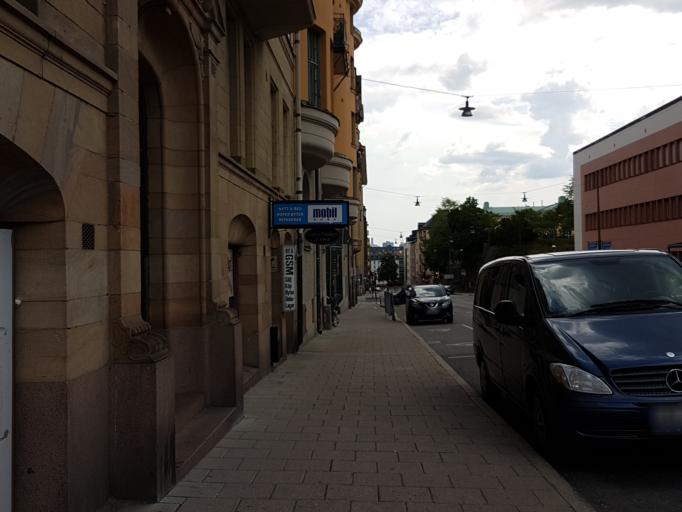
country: SE
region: Stockholm
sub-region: Stockholms Kommun
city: Stockholm
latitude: 59.3389
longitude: 18.0487
